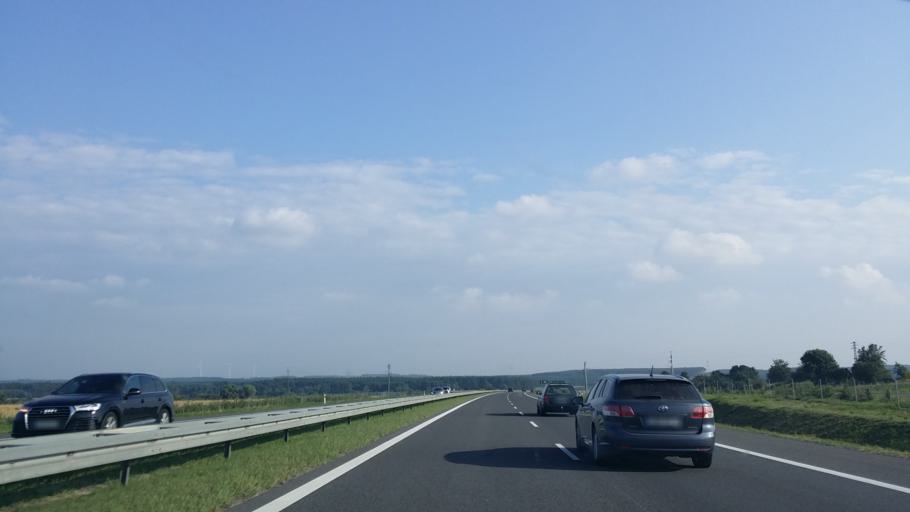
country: PL
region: Lubusz
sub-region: Powiat miedzyrzecki
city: Miedzyrzecz
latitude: 52.3498
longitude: 15.5564
